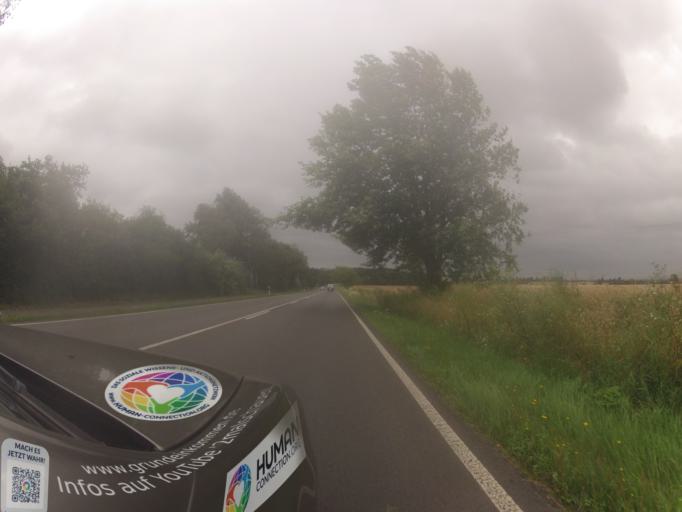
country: DE
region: Mecklenburg-Vorpommern
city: Pasewalk
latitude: 53.4820
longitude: 13.9829
